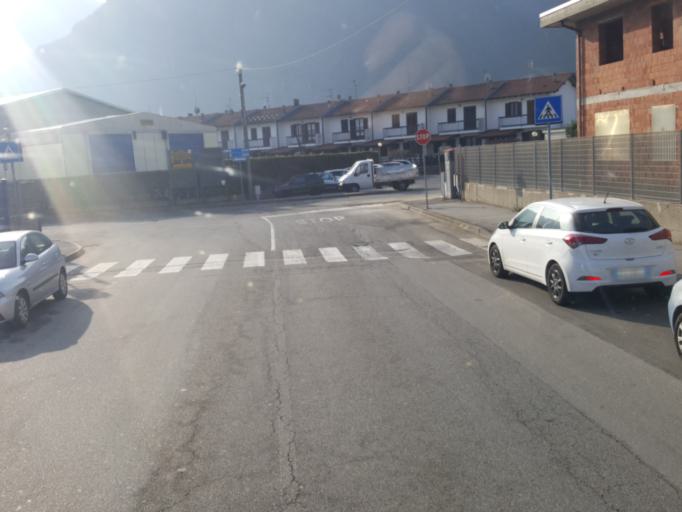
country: IT
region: Piedmont
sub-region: Provincia Verbano-Cusio-Ossola
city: Gravellona Toce
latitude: 45.9302
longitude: 8.4439
